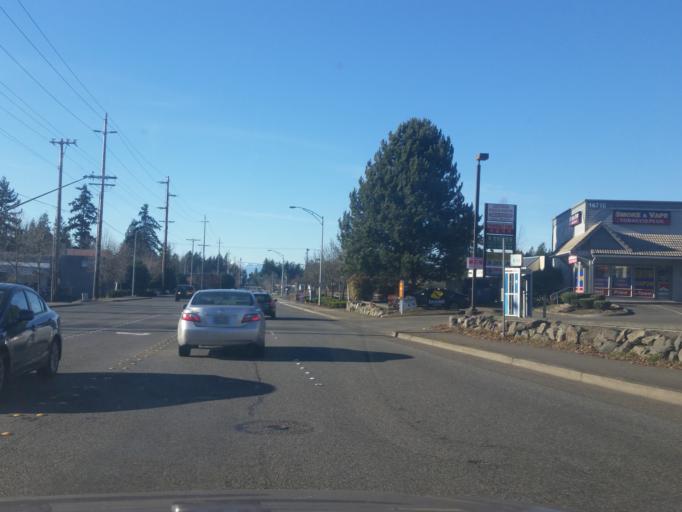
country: US
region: Washington
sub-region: Snohomish County
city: Alderwood Manor
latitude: 47.8465
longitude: -122.2951
